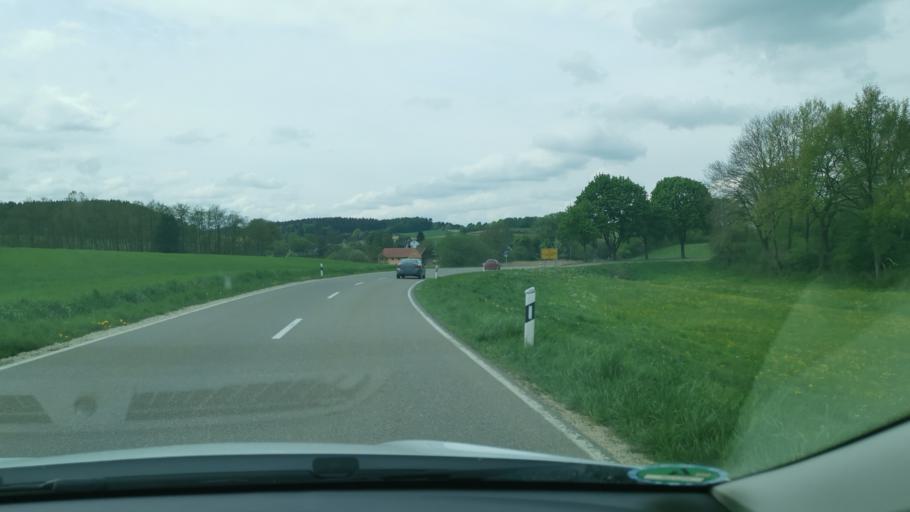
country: DE
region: Bavaria
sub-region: Swabia
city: Schiltberg
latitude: 48.4502
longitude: 11.2516
